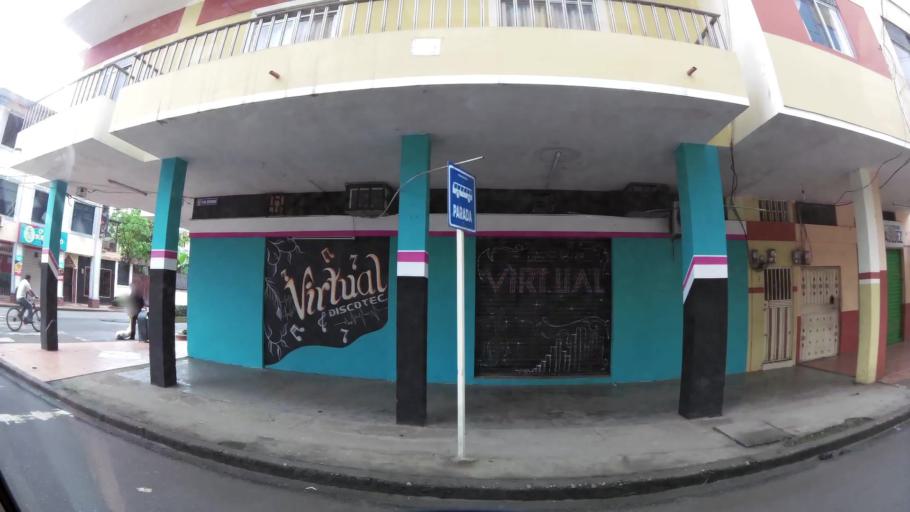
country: EC
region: El Oro
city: Pasaje
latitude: -3.3271
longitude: -79.8052
